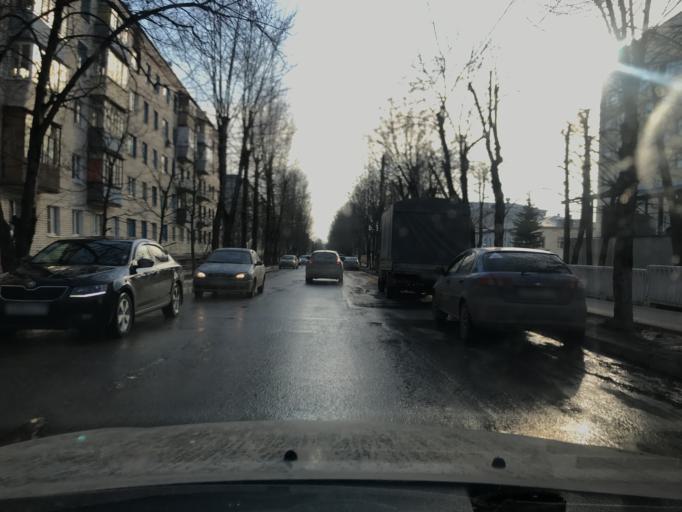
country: RU
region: Kaluga
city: Kaluga
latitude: 54.5181
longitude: 36.2405
